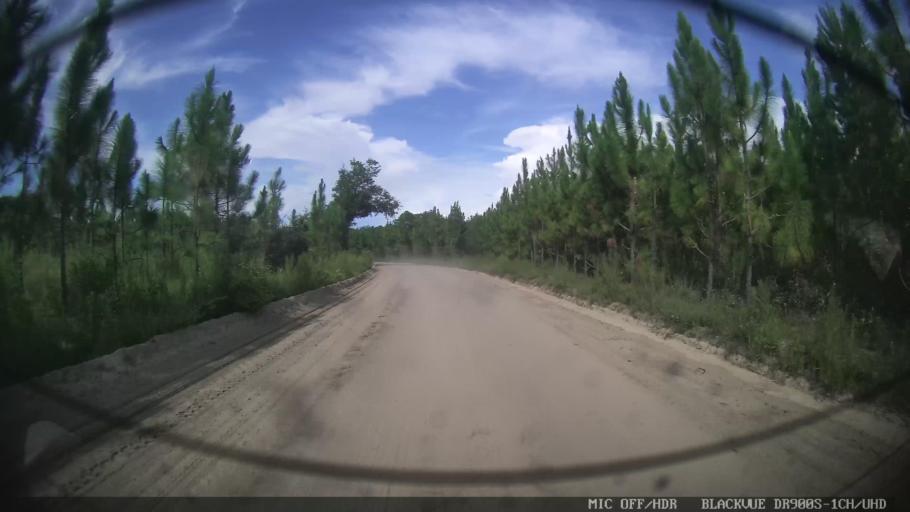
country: US
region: Georgia
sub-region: Echols County
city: Statenville
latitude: 30.6202
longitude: -83.2149
